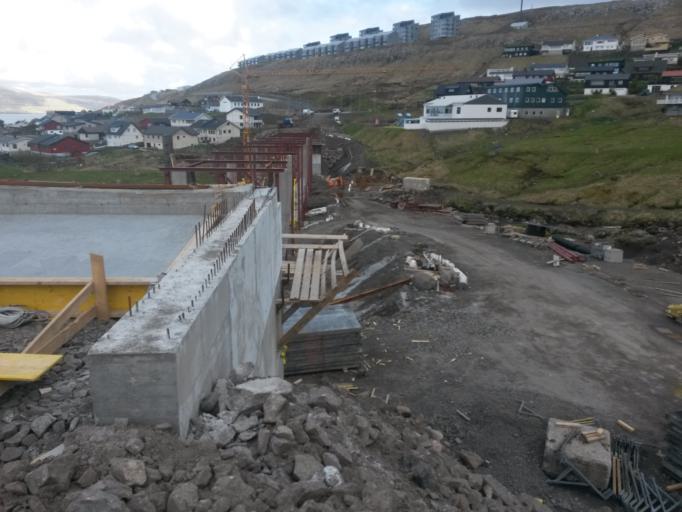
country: FO
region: Streymoy
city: Argir
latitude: 61.9981
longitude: -6.7939
